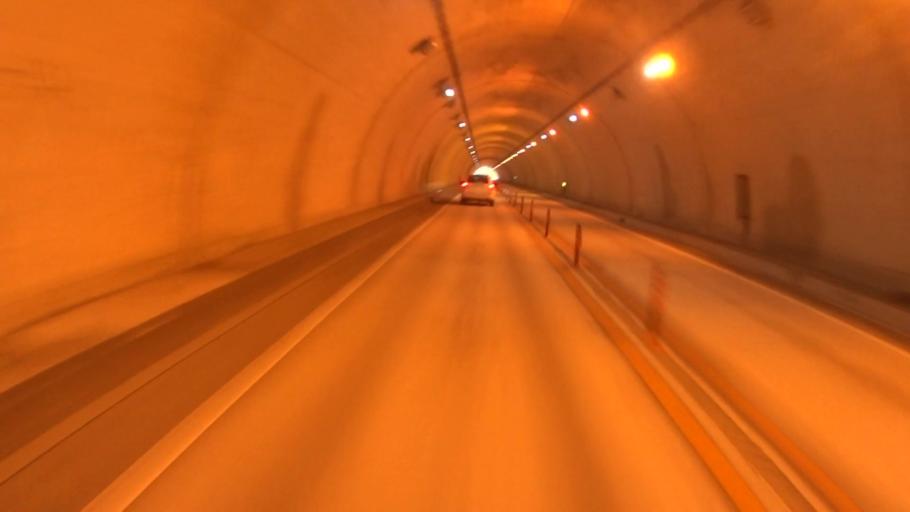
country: JP
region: Kyoto
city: Ayabe
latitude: 35.3465
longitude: 135.2961
